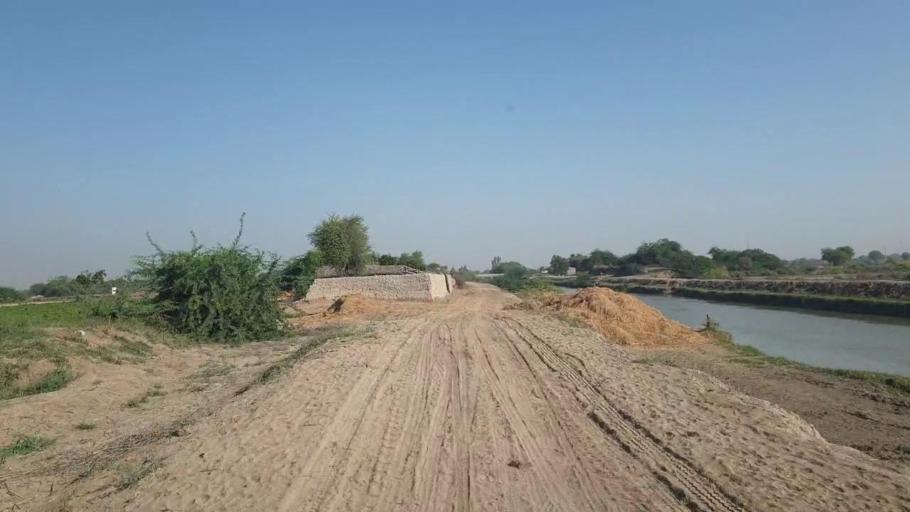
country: PK
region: Sindh
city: Badin
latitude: 24.7286
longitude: 68.8047
